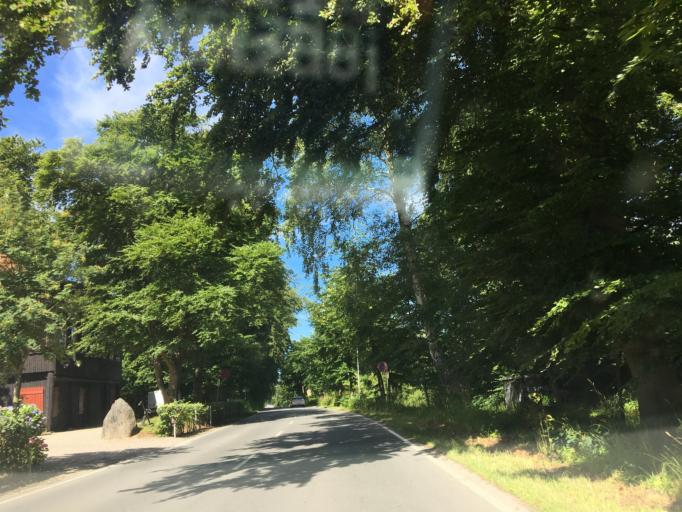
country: DK
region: South Denmark
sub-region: Svendborg Kommune
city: Thuro By
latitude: 55.0603
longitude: 10.6436
